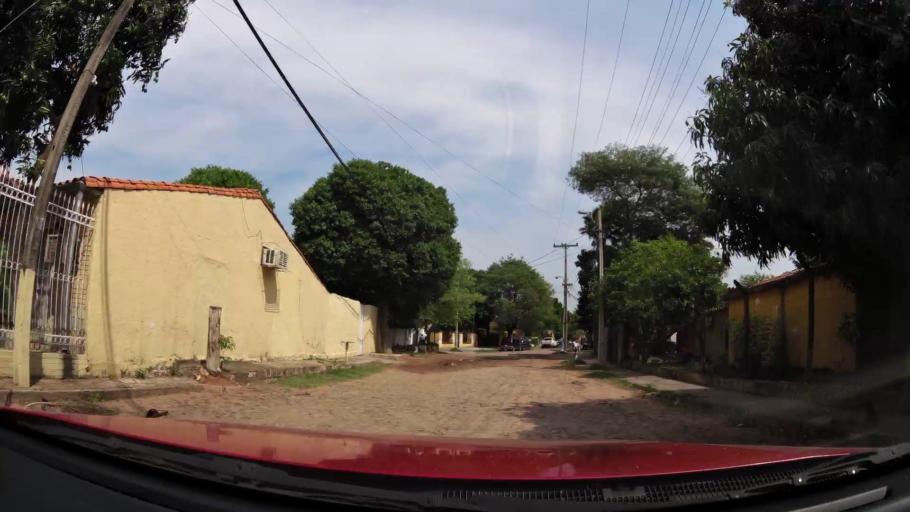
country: PY
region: Asuncion
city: Asuncion
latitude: -25.2611
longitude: -57.5836
